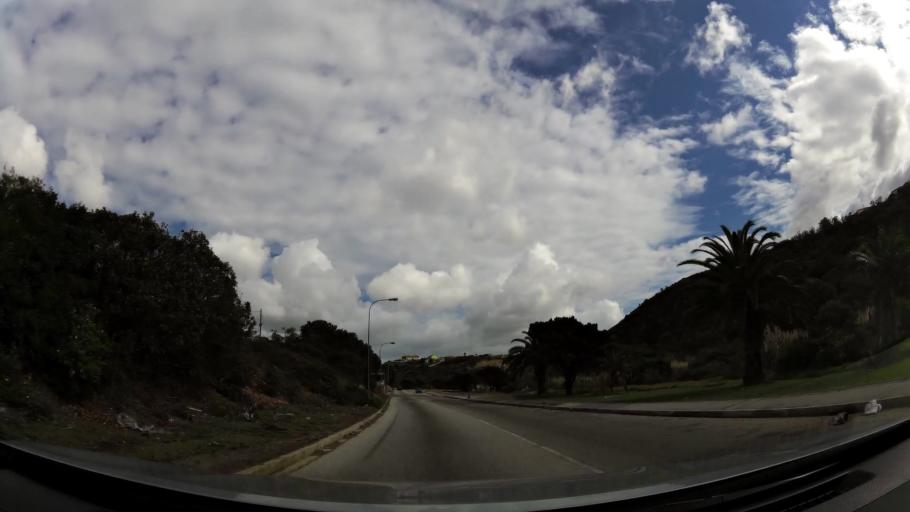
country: ZA
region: Eastern Cape
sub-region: Nelson Mandela Bay Metropolitan Municipality
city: Port Elizabeth
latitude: -33.9300
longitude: 25.5562
